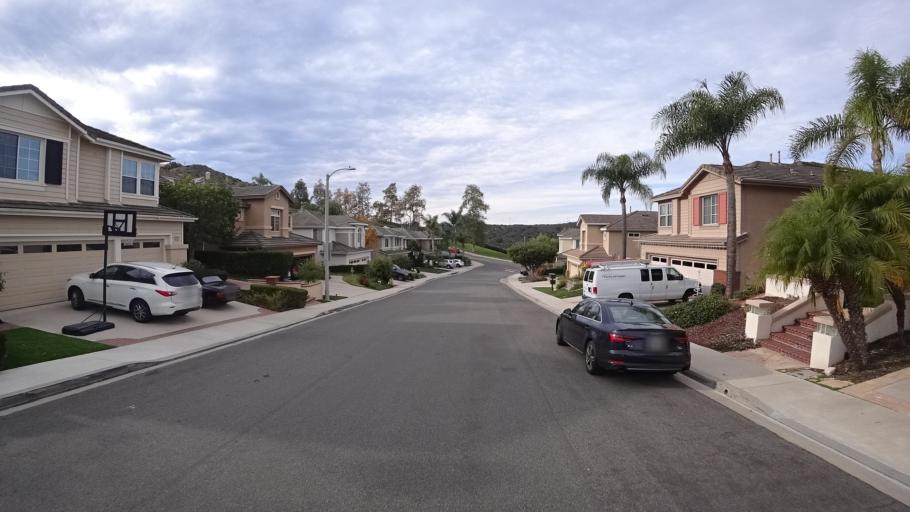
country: US
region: California
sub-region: Orange County
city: Aliso Viejo
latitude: 33.5799
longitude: -117.7433
